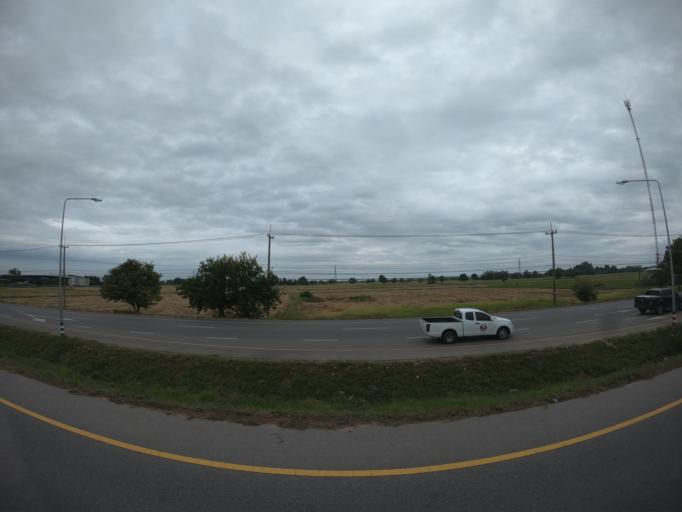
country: TH
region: Maha Sarakham
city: Maha Sarakham
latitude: 16.1505
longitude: 103.3861
